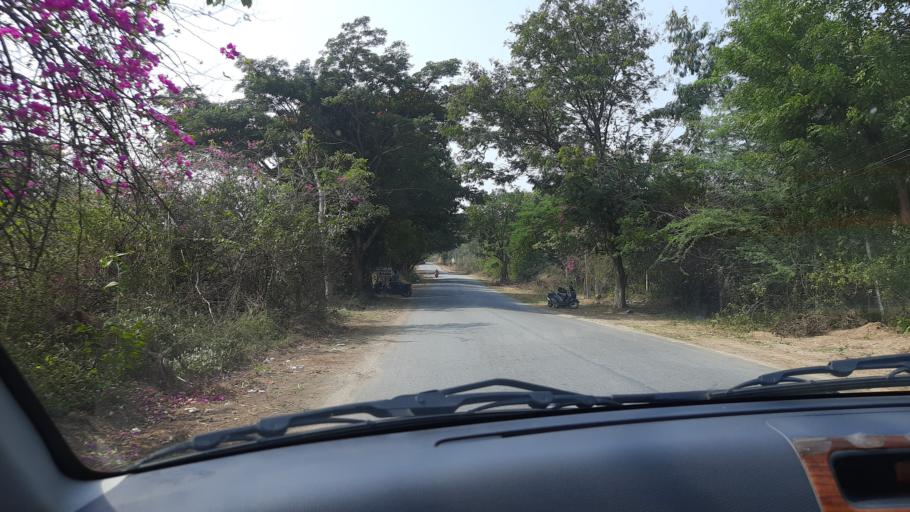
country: IN
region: Telangana
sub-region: Rangareddi
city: Lal Bahadur Nagar
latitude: 17.2753
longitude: 78.6639
